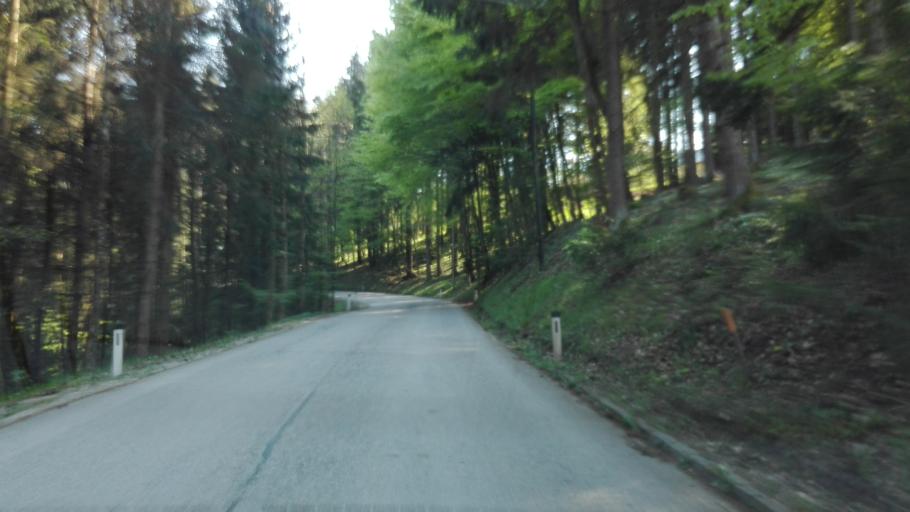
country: AT
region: Upper Austria
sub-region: Politischer Bezirk Rohrbach
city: Atzesberg
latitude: 48.4296
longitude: 13.9203
